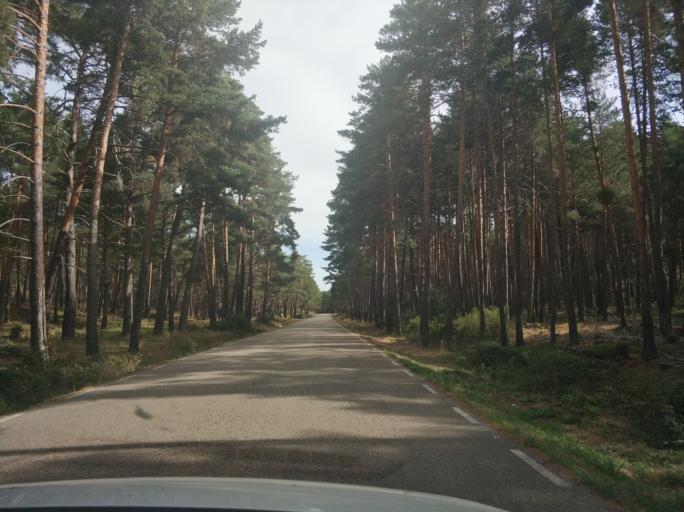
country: ES
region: Castille and Leon
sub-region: Provincia de Soria
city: Navaleno
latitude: 41.8438
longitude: -2.9936
